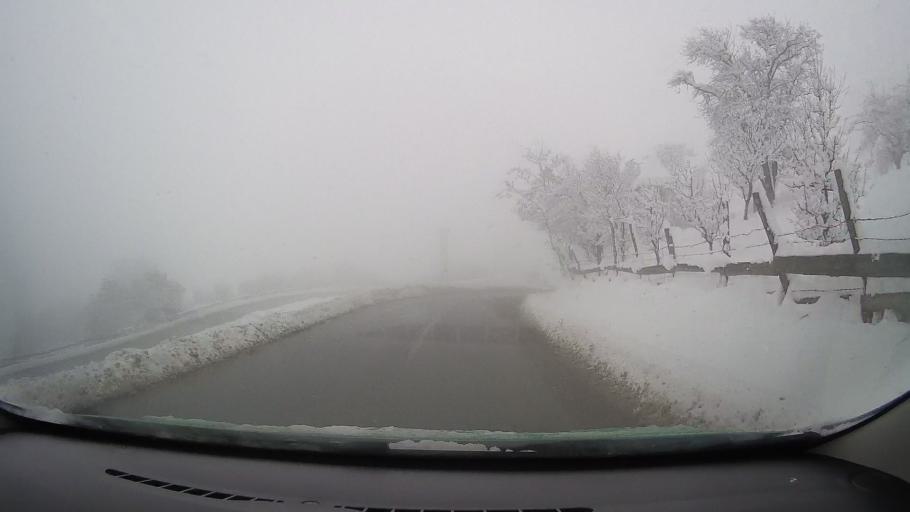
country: RO
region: Sibiu
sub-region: Comuna Jina
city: Jina
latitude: 45.7841
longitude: 23.6905
